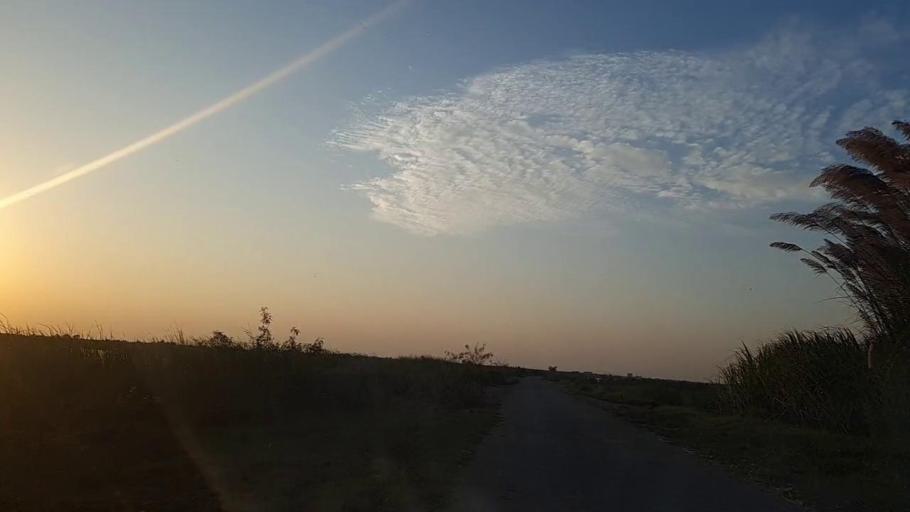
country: PK
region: Sindh
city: Chuhar Jamali
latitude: 24.4625
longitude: 68.1057
